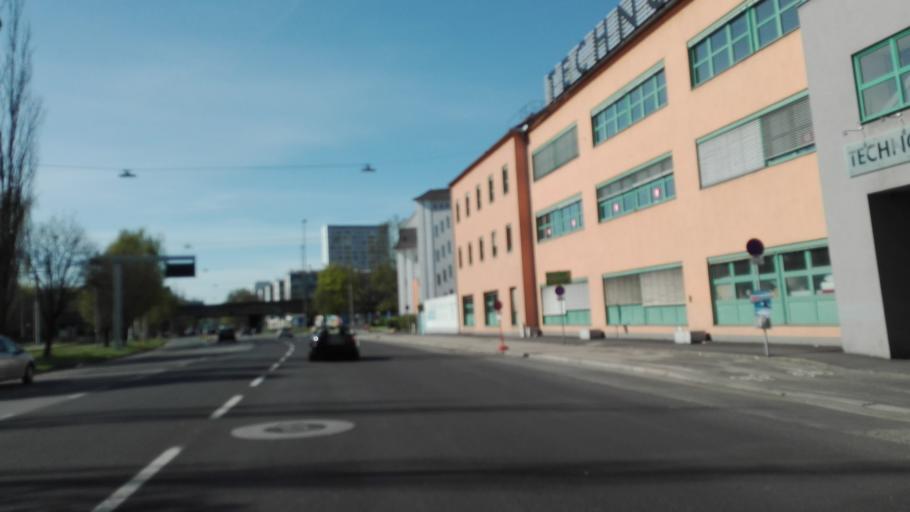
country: AT
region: Upper Austria
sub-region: Linz Stadt
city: Linz
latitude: 48.2814
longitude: 14.3085
